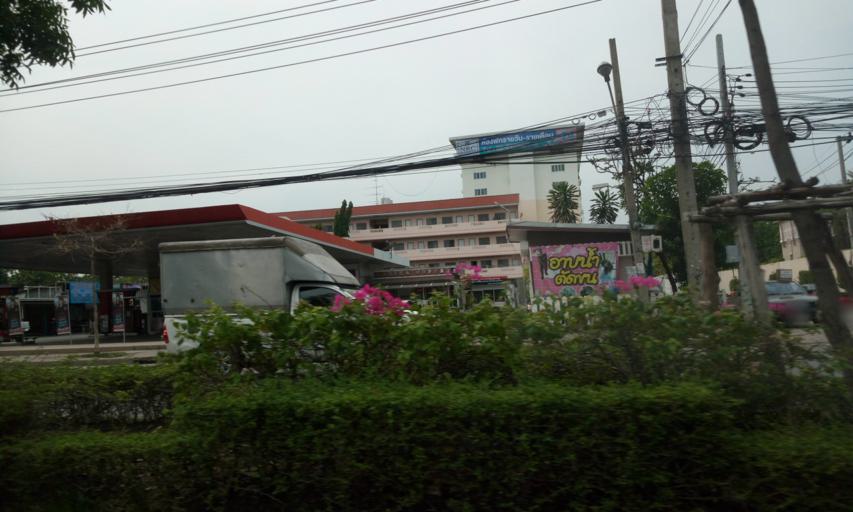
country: TH
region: Bangkok
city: Saphan Sung
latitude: 13.7222
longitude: 100.7159
